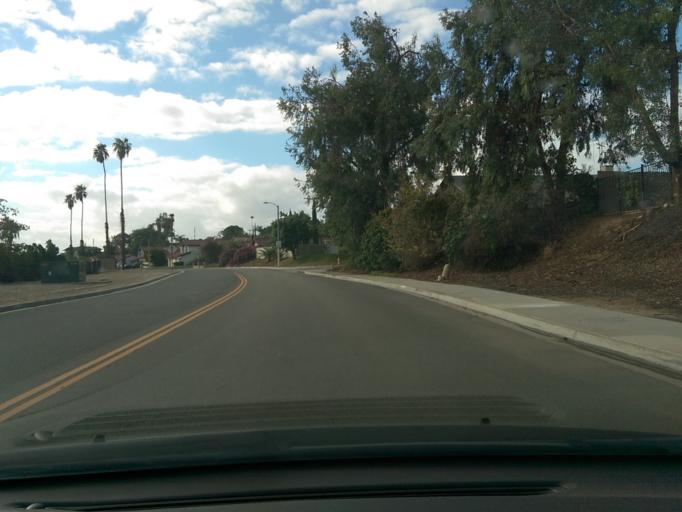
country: US
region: California
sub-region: Riverside County
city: Sunnyslope
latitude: 33.9937
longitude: -117.4297
